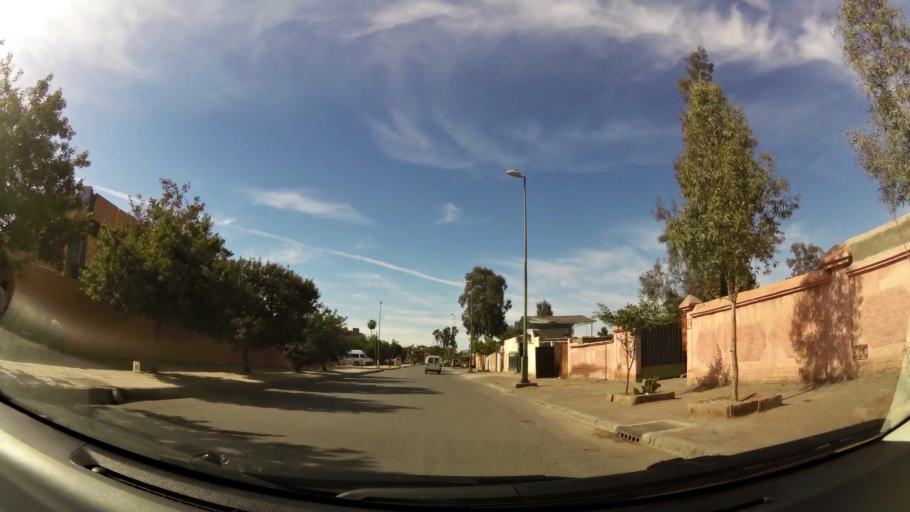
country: MA
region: Marrakech-Tensift-Al Haouz
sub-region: Marrakech
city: Marrakesh
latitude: 31.6085
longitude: -7.9571
